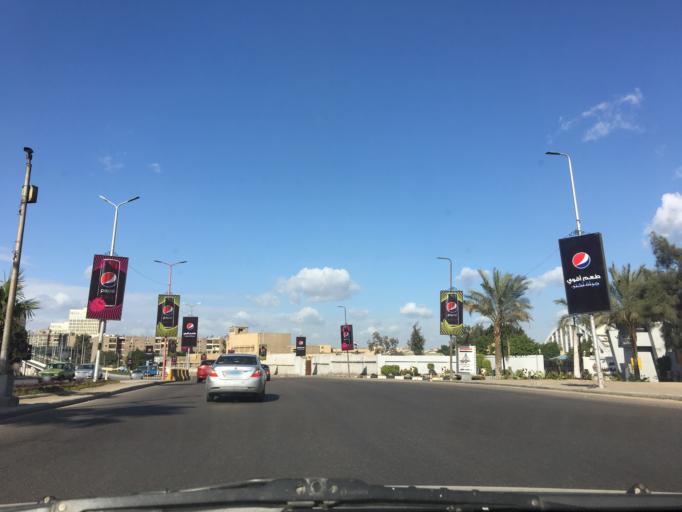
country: EG
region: Muhafazat al Qahirah
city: Cairo
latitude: 30.0556
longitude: 31.3068
